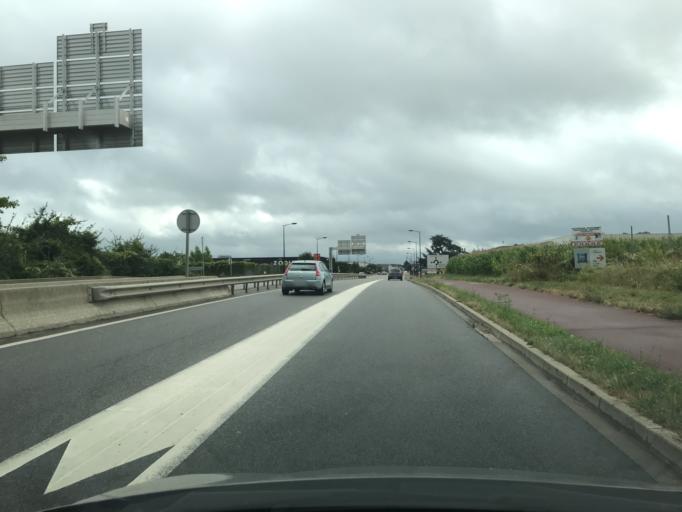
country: FR
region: Ile-de-France
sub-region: Departement des Yvelines
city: Chambourcy
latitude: 48.9124
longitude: 2.0280
